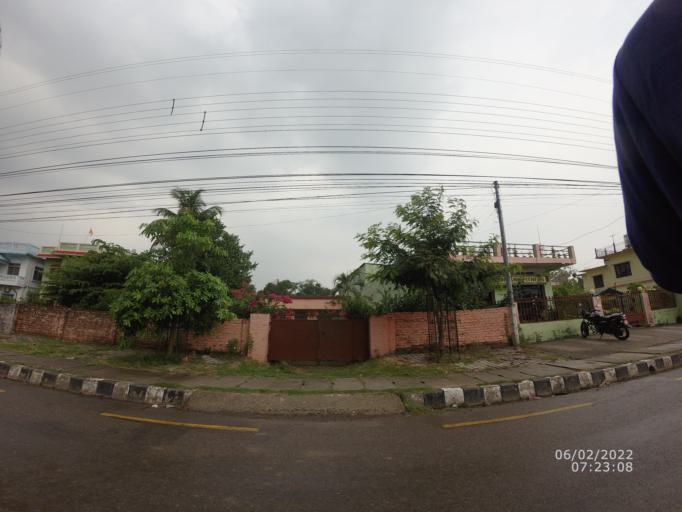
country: NP
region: Western Region
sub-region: Lumbini Zone
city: Bhairahawa
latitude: 27.4940
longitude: 83.4459
